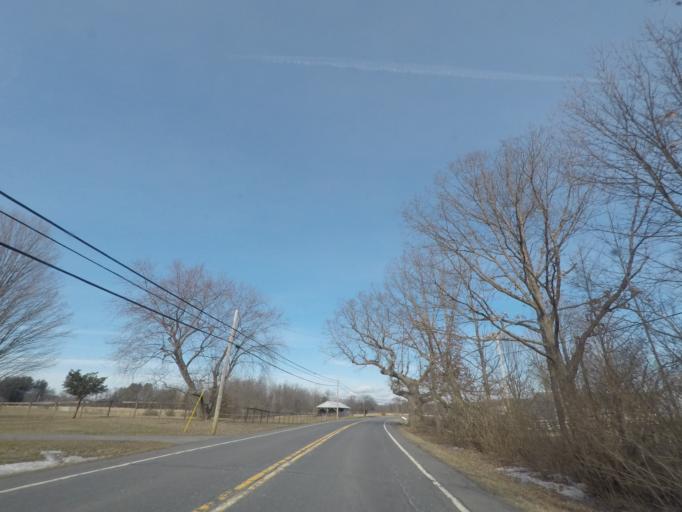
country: US
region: New York
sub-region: Rensselaer County
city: Nassau
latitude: 42.4958
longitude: -73.6230
